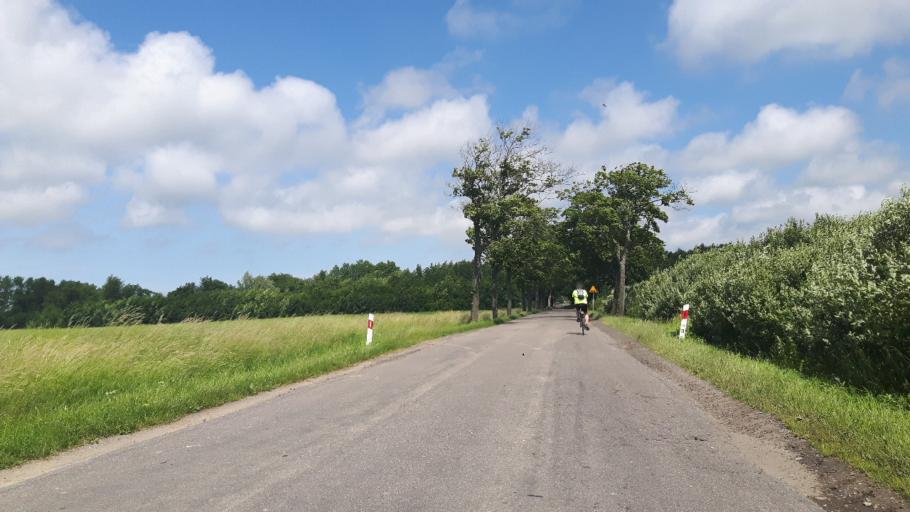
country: PL
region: Pomeranian Voivodeship
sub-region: Powiat slupski
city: Ustka
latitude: 54.5307
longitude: 16.8158
